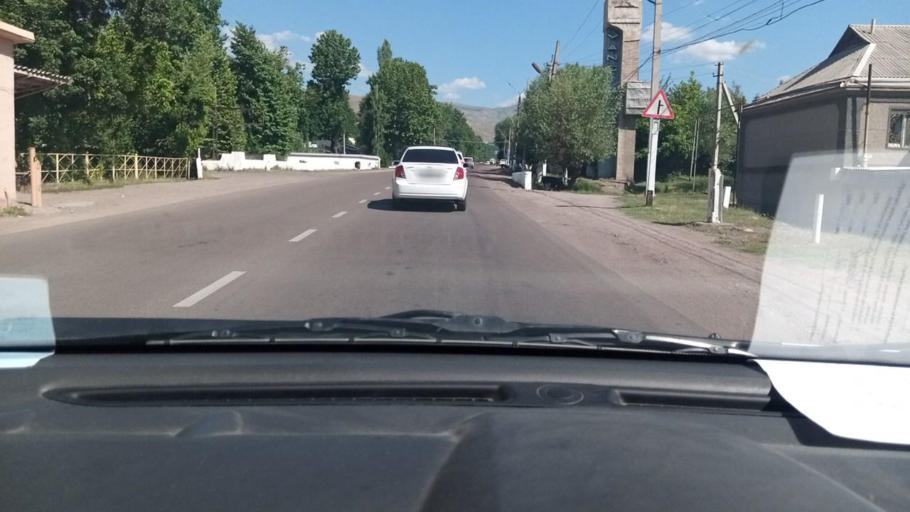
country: UZ
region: Toshkent
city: Angren
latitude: 41.0396
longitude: 70.0938
